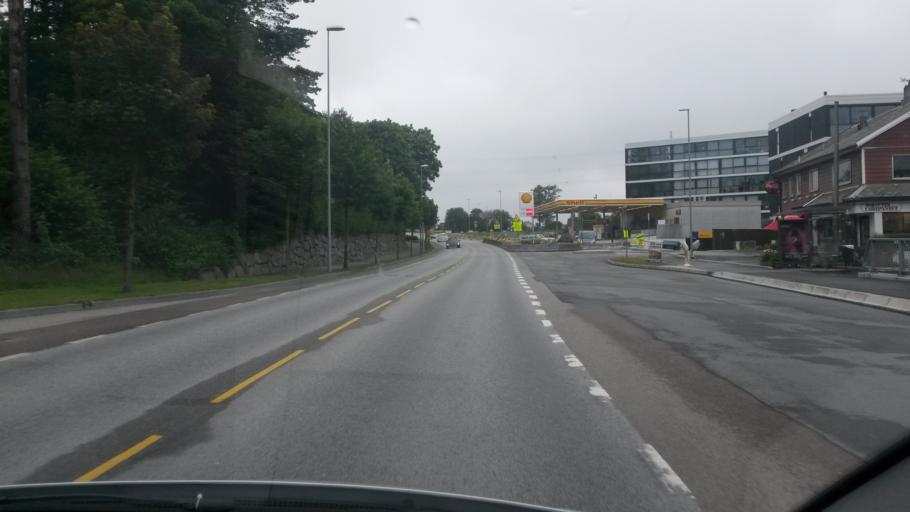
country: NO
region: Rogaland
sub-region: Sandnes
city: Sandnes
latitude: 58.8337
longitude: 5.7194
